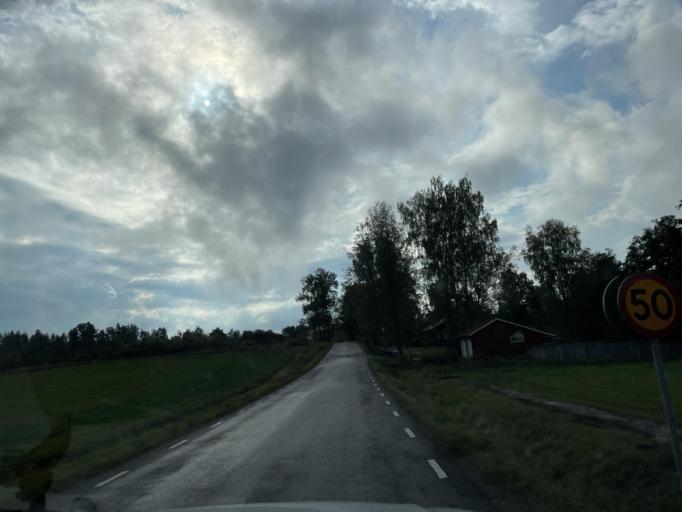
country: SE
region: Vaermland
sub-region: Karlstads Kommun
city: Skattkarr
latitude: 59.4177
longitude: 13.6071
